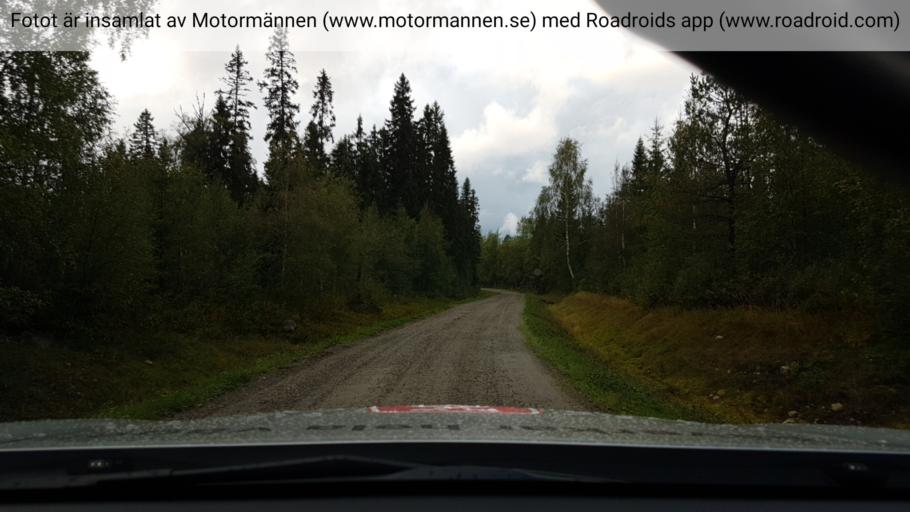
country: SE
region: Vaesterbotten
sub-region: Asele Kommun
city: Asele
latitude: 64.1481
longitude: 16.9302
